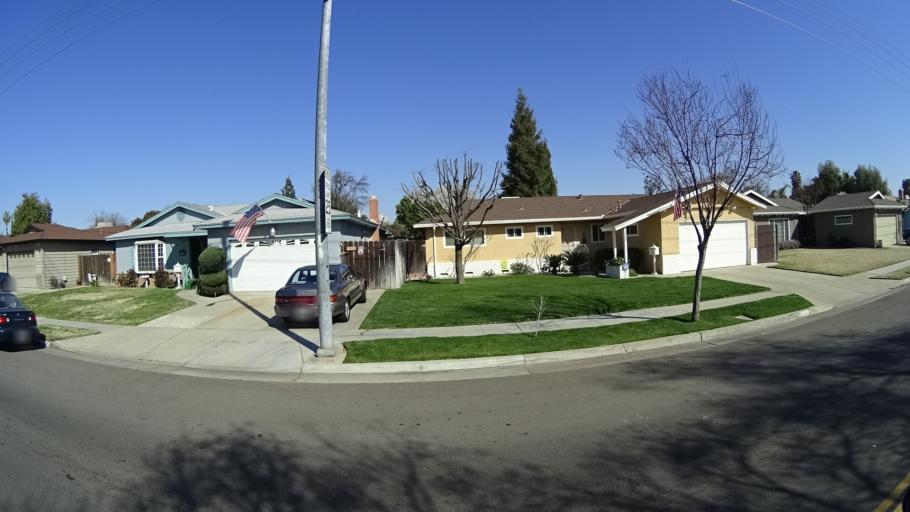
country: US
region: California
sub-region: Fresno County
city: Clovis
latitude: 36.8303
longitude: -119.7598
